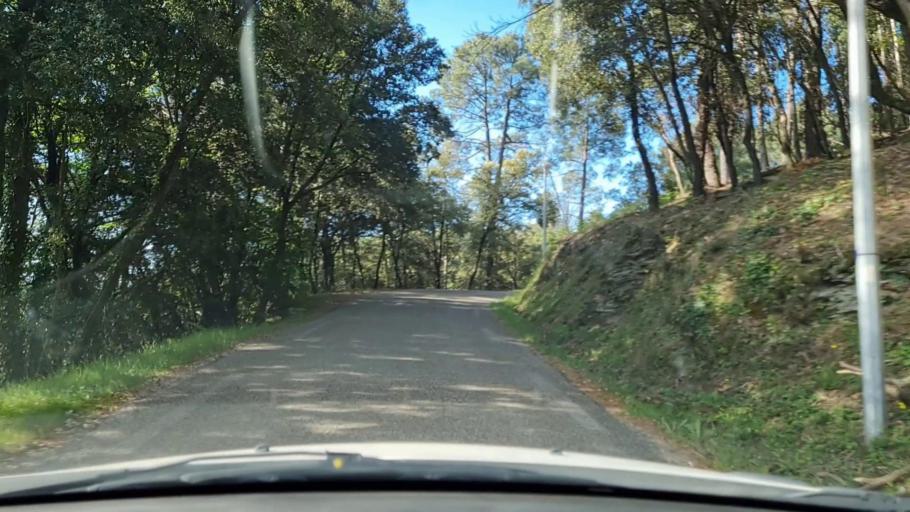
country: FR
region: Languedoc-Roussillon
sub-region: Departement du Gard
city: Les Salles-du-Gardon
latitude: 44.1845
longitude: 4.0110
